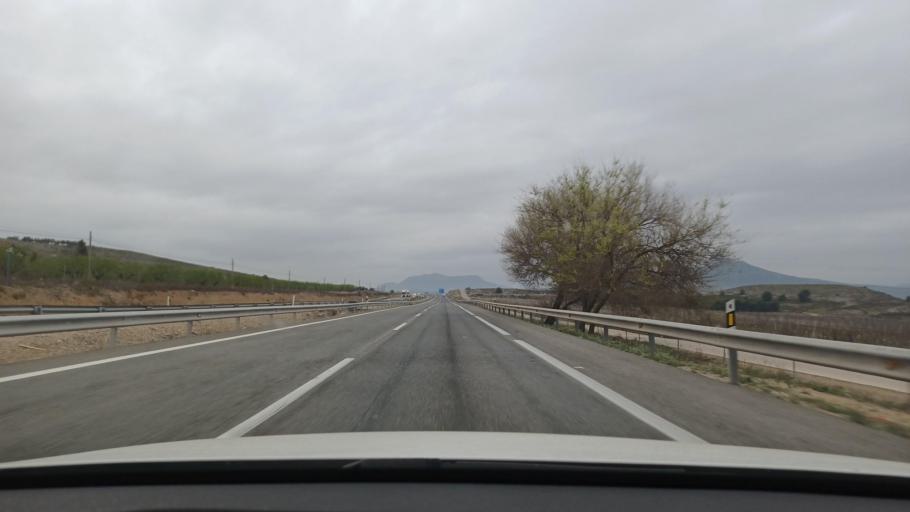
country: ES
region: Valencia
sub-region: Provincia de Alicante
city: Villena
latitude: 38.5884
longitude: -0.8440
